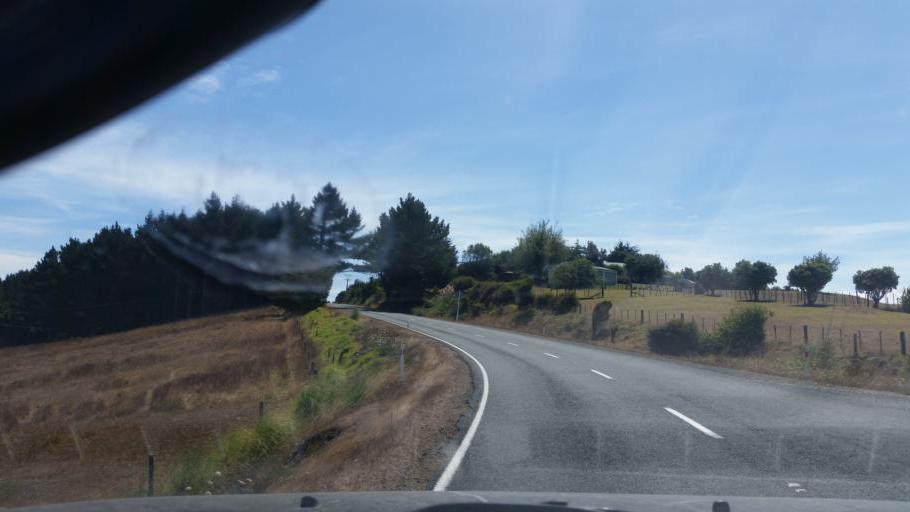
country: NZ
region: Auckland
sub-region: Auckland
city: Wellsford
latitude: -36.1934
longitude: 174.1615
